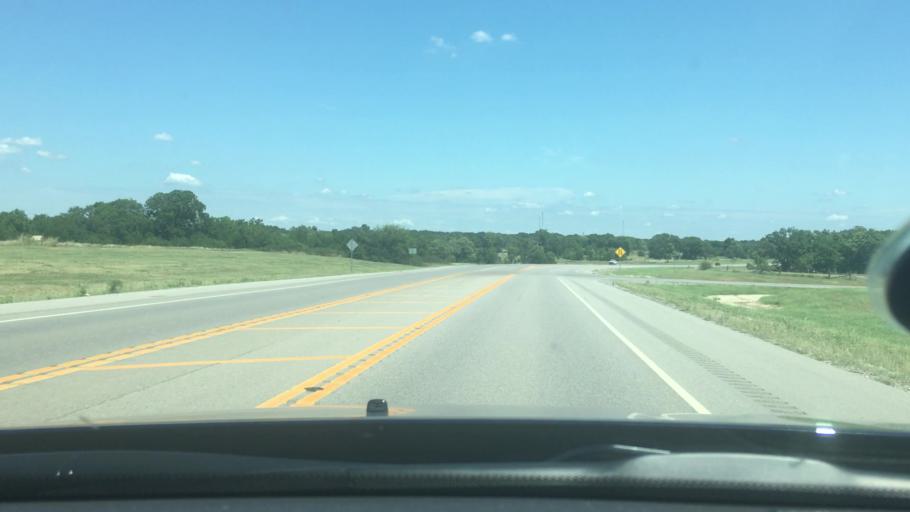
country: US
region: Oklahoma
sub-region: Bryan County
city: Durant
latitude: 33.9888
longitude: -96.3396
